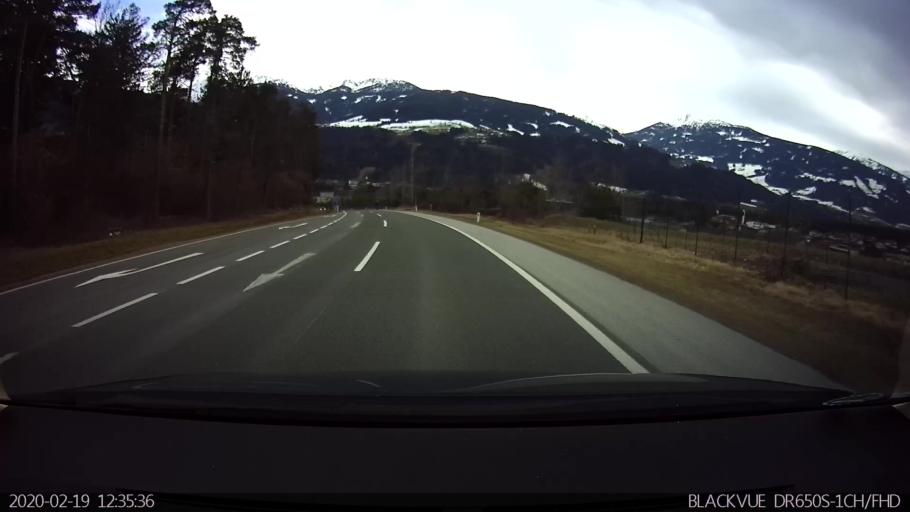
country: AT
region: Tyrol
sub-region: Politischer Bezirk Schwaz
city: Vomp
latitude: 47.3325
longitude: 11.6729
